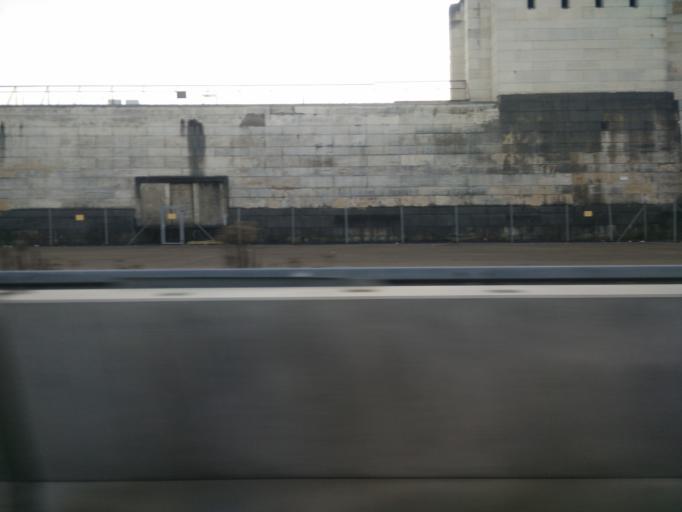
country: DE
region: Bavaria
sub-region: Regierungsbezirk Mittelfranken
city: Nuernberg
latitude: 49.4317
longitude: 11.1257
